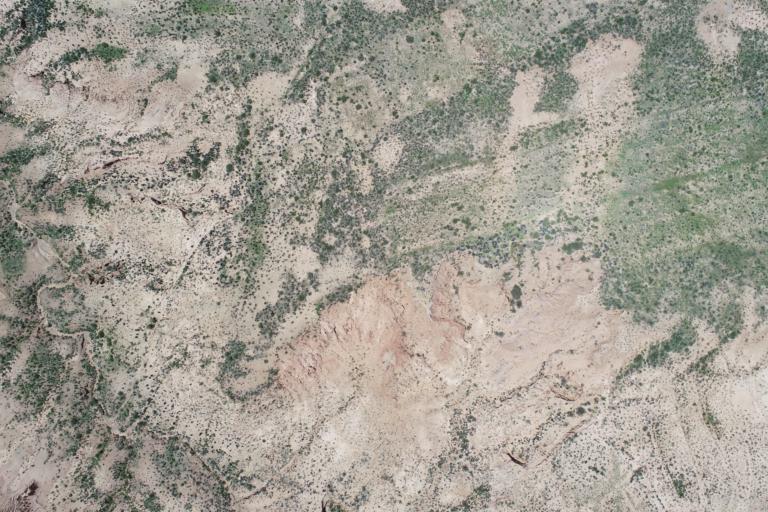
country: BO
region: La Paz
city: Curahuara de Carangas
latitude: -17.3282
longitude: -68.5105
